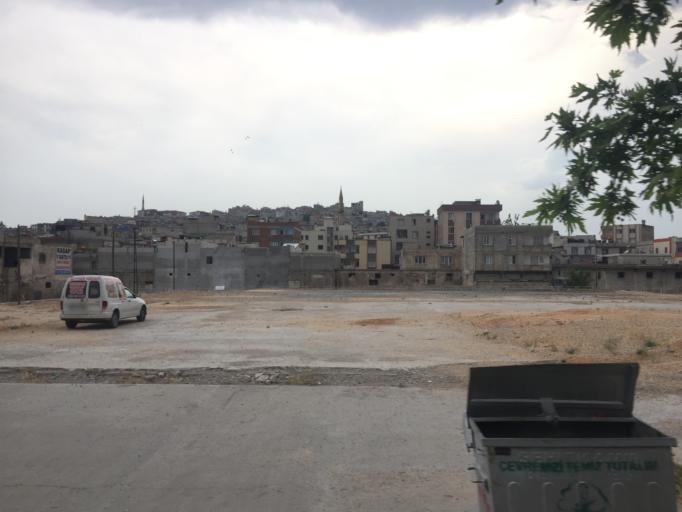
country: TR
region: Gaziantep
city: Gaziantep
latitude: 37.0722
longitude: 37.4131
